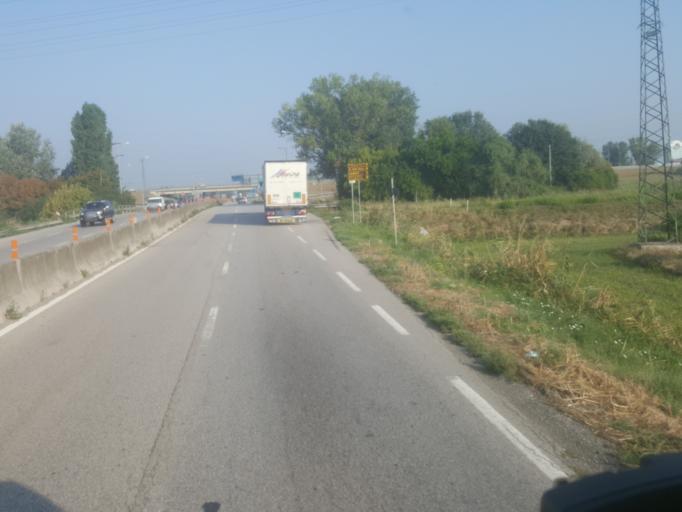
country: IT
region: Emilia-Romagna
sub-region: Provincia di Ravenna
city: Fornace Zarattini
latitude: 44.4258
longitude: 12.1579
